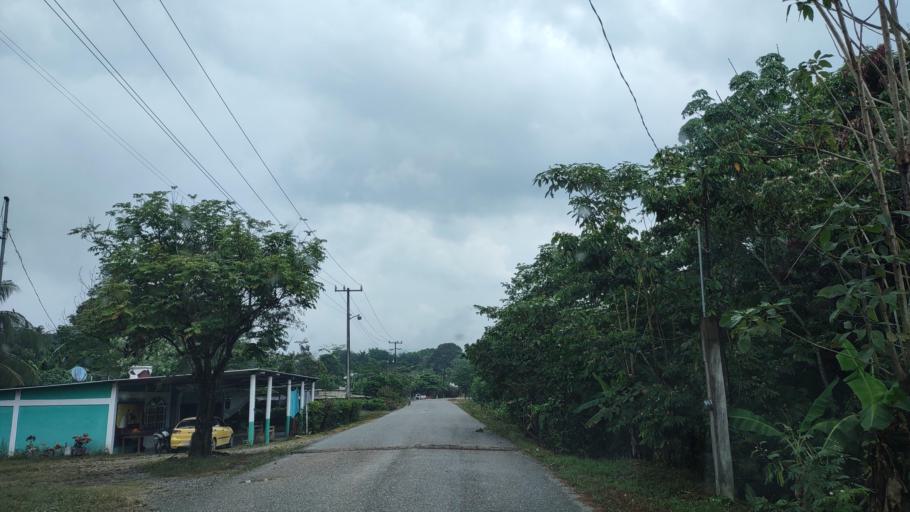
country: MX
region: Veracruz
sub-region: Uxpanapa
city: Poblado 10
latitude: 17.4728
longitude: -94.1210
